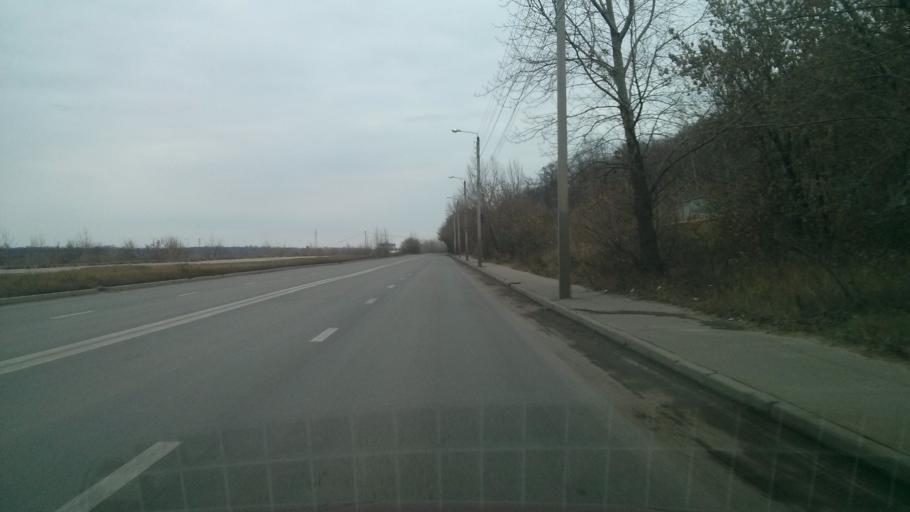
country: RU
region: Nizjnij Novgorod
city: Bor
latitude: 56.3159
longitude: 44.0823
